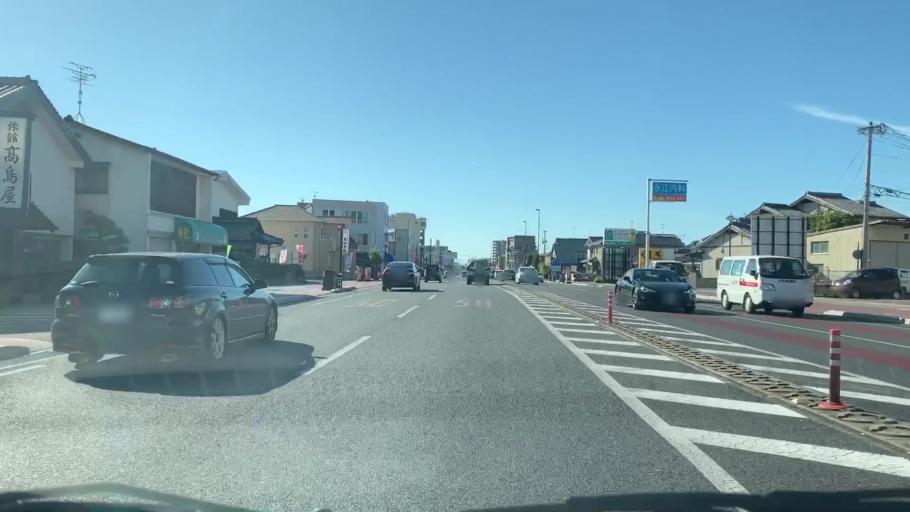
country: JP
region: Saga Prefecture
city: Saga-shi
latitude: 33.2700
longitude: 130.2939
